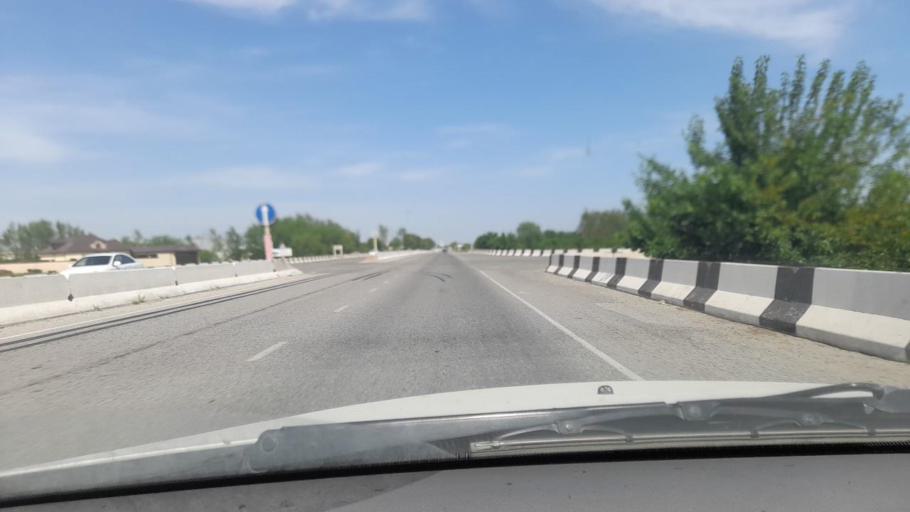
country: UZ
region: Samarqand
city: Kattaqo'rg'on
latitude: 39.9334
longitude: 66.3684
